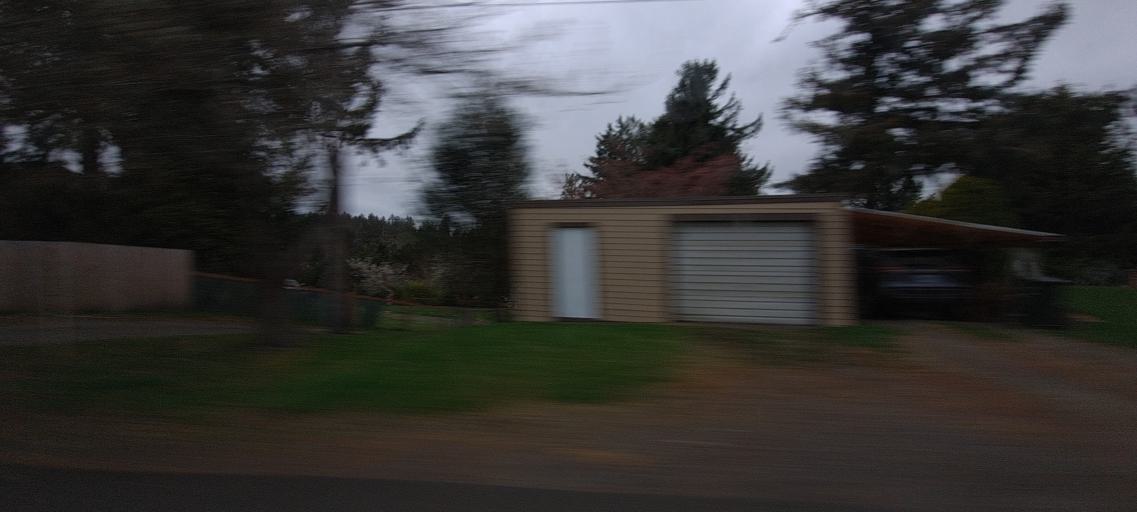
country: US
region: Oregon
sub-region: Clatsop County
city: Warrenton
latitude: 46.1376
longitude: -123.9310
